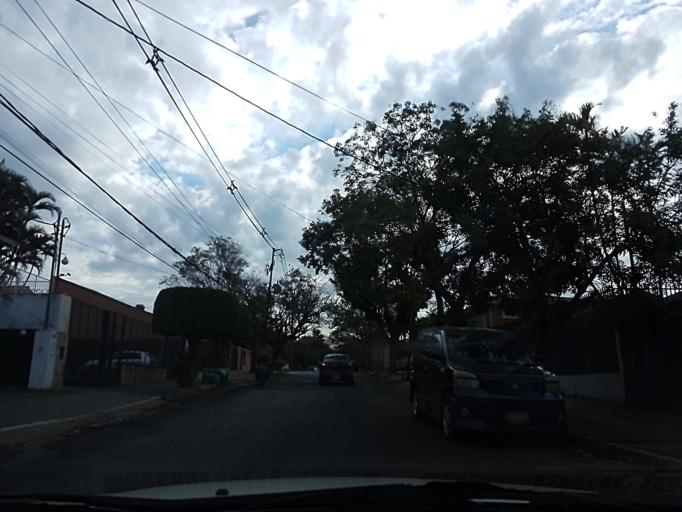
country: PY
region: Asuncion
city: Asuncion
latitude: -25.3000
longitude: -57.5960
